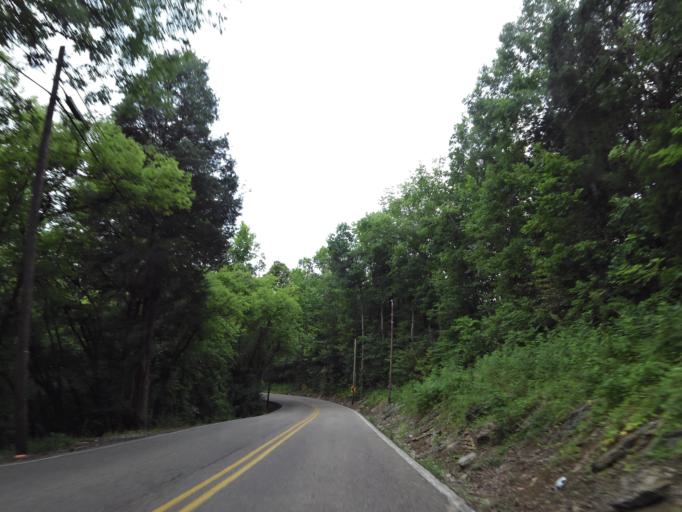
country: US
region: Tennessee
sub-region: Knox County
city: Knoxville
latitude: 35.9368
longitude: -83.8705
